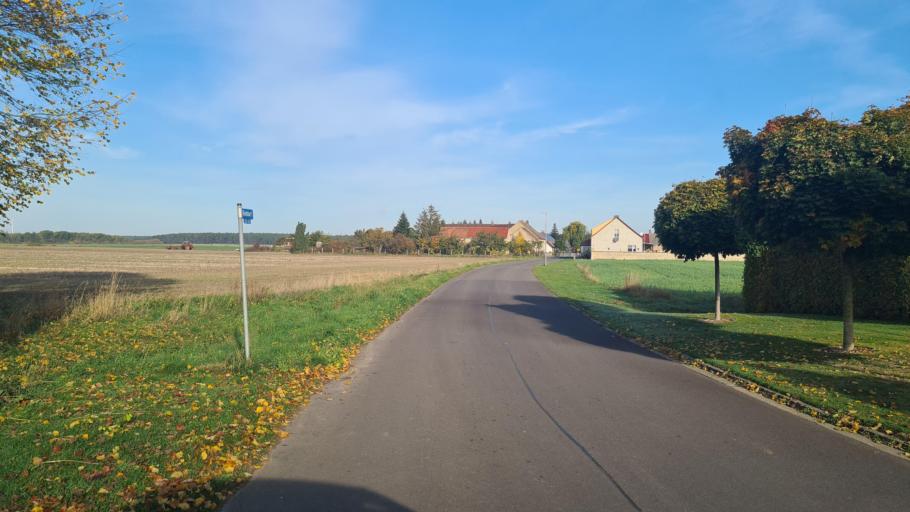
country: DE
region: Brandenburg
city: Ihlow
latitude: 51.8868
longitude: 13.3770
